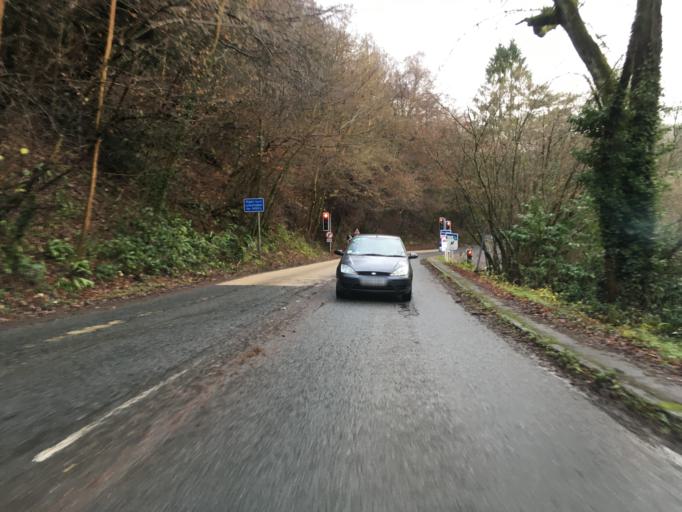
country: GB
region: England
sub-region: Gloucestershire
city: Minchinhampton
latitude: 51.6910
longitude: -2.1960
